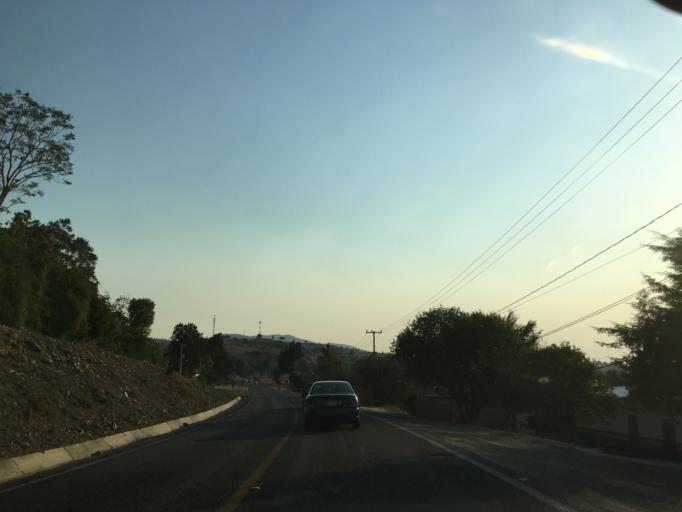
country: MX
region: Michoacan
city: Charo
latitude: 19.7393
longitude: -101.0808
